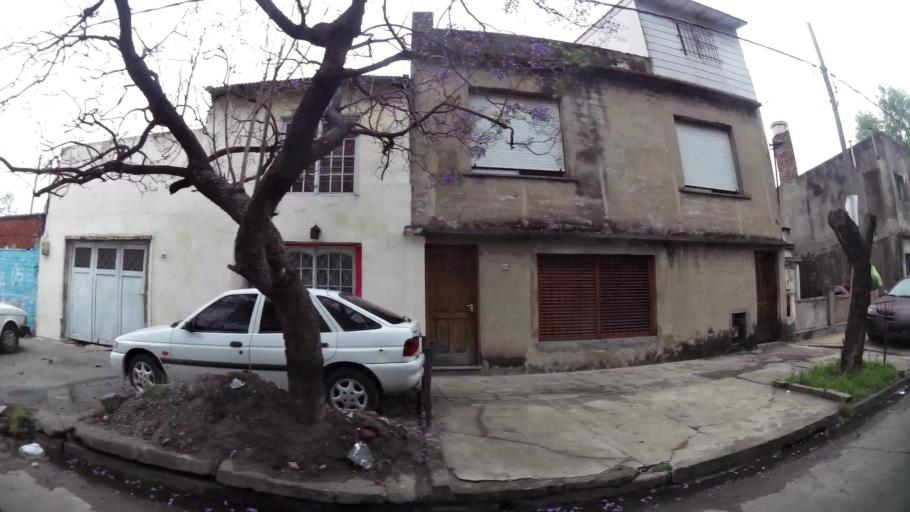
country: AR
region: Buenos Aires
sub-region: Partido de Lanus
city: Lanus
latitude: -34.7174
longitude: -58.3644
